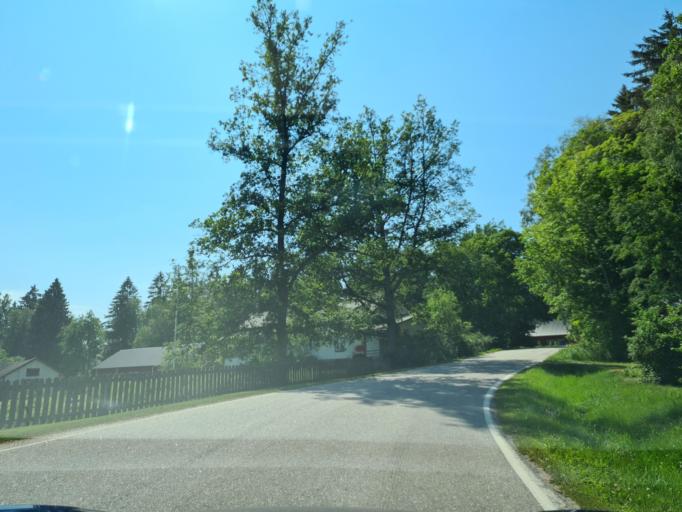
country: FI
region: Varsinais-Suomi
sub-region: Turku
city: Tarvasjoki
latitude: 60.5959
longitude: 22.6672
